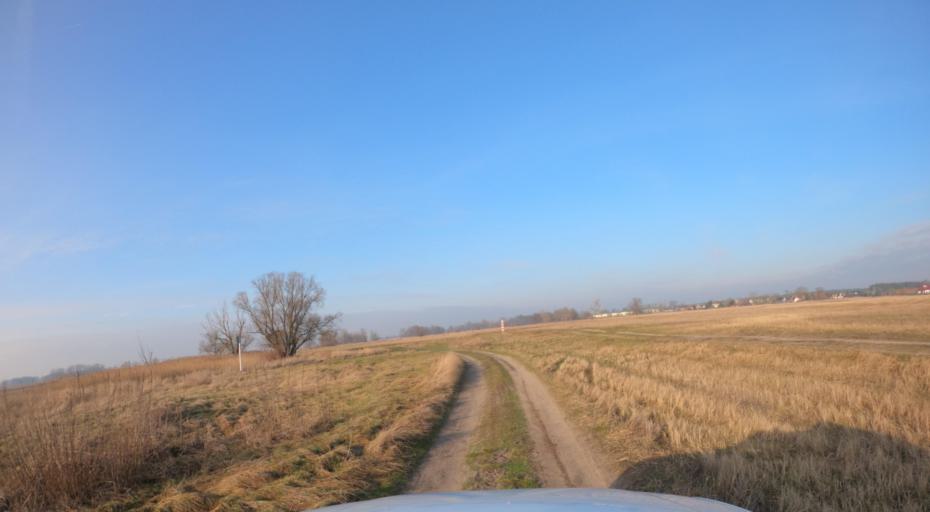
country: PL
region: Lubusz
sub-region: Powiat gorzowski
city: Kostrzyn nad Odra
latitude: 52.6153
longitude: 14.5886
